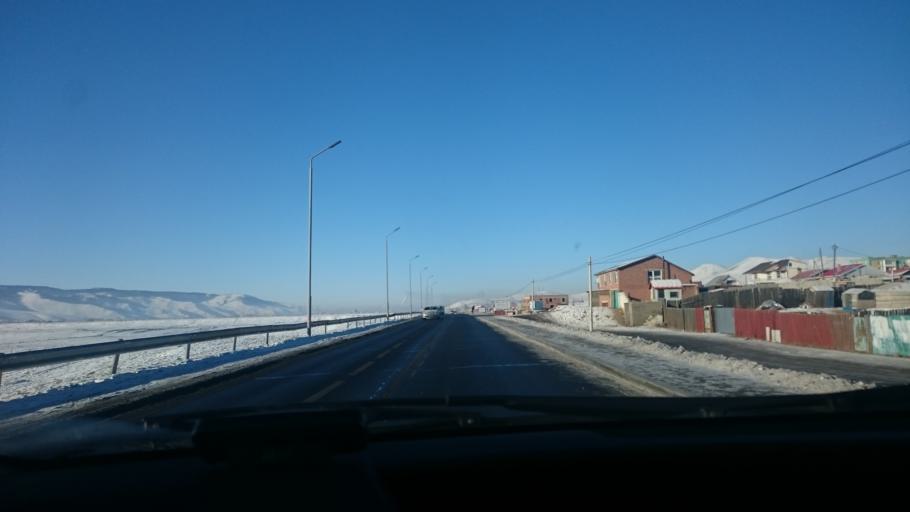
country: MN
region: Ulaanbaatar
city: Ulaanbaatar
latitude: 47.9159
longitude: 107.0891
